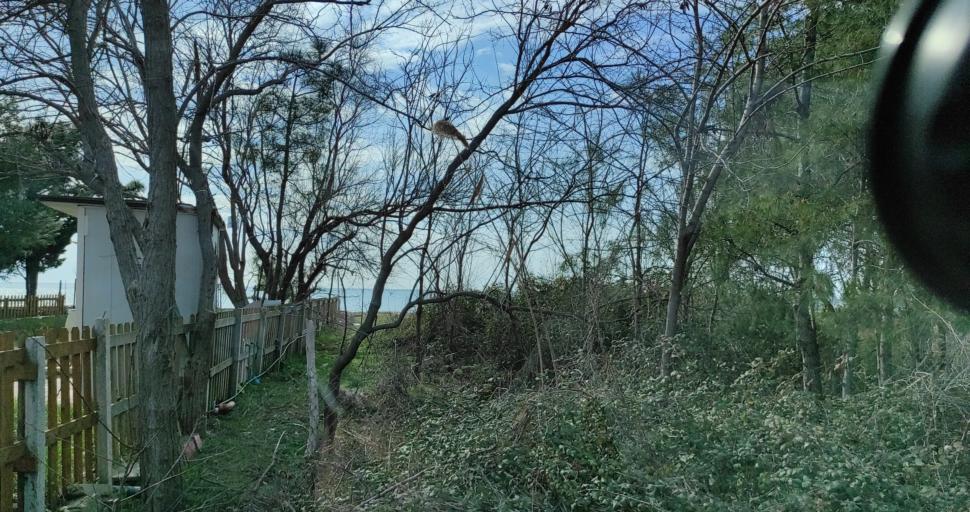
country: AL
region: Lezhe
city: Shengjin
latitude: 41.7843
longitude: 19.6032
